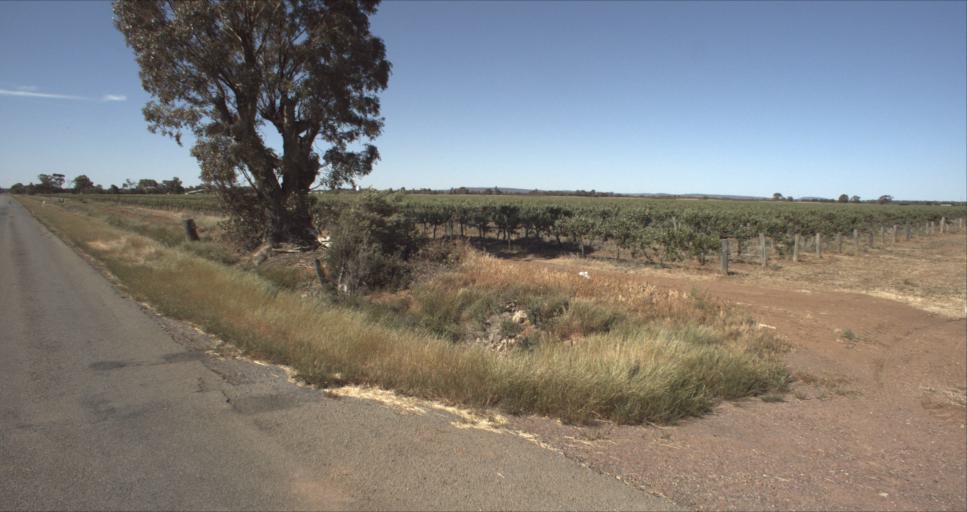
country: AU
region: New South Wales
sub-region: Leeton
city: Leeton
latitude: -34.5784
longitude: 146.3803
